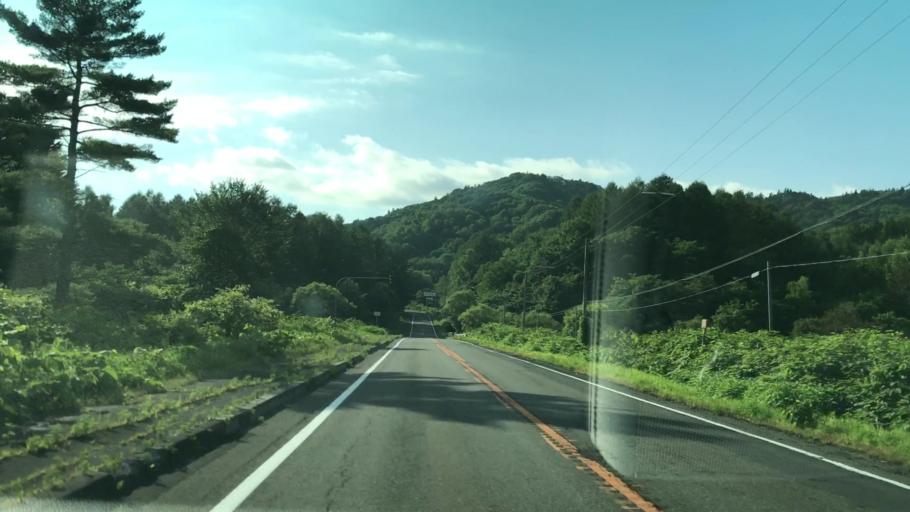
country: JP
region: Hokkaido
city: Chitose
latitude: 42.8705
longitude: 142.1535
